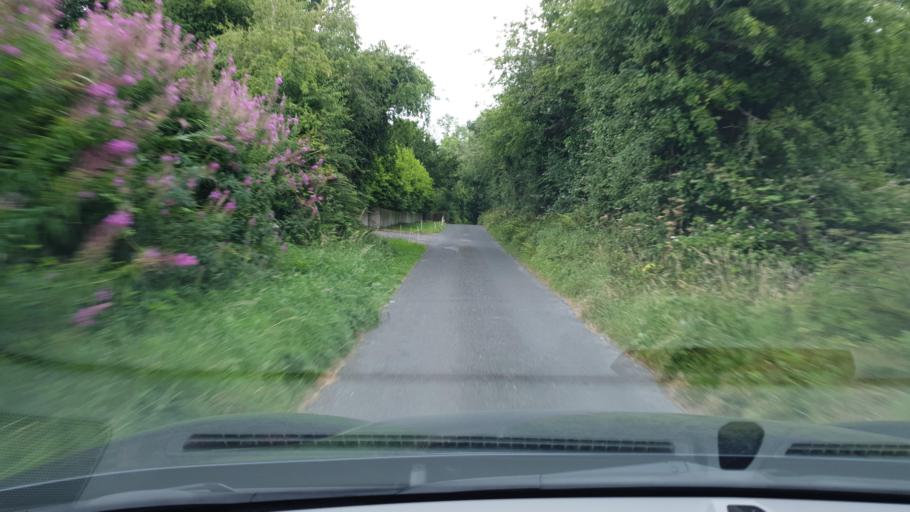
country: IE
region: Leinster
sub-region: An Mhi
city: Ashbourne
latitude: 53.5630
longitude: -6.3881
